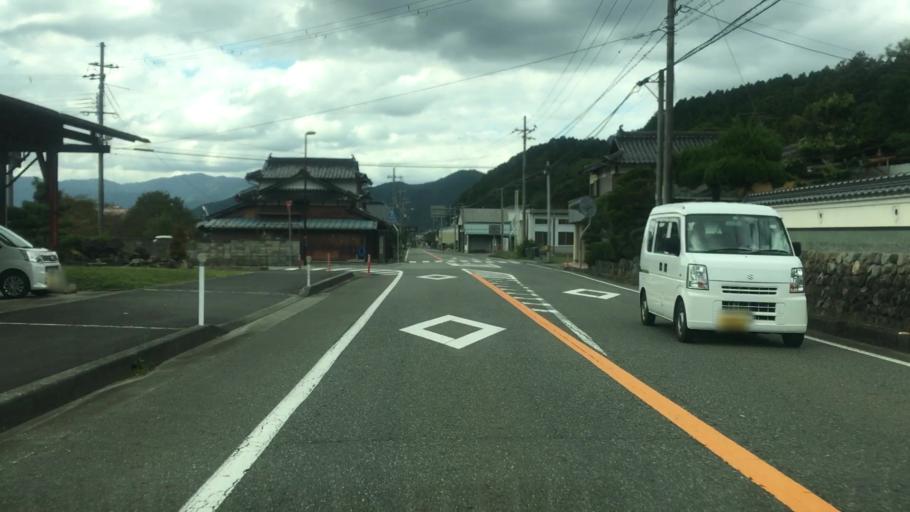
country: JP
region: Kyoto
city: Fukuchiyama
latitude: 35.3070
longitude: 134.9059
